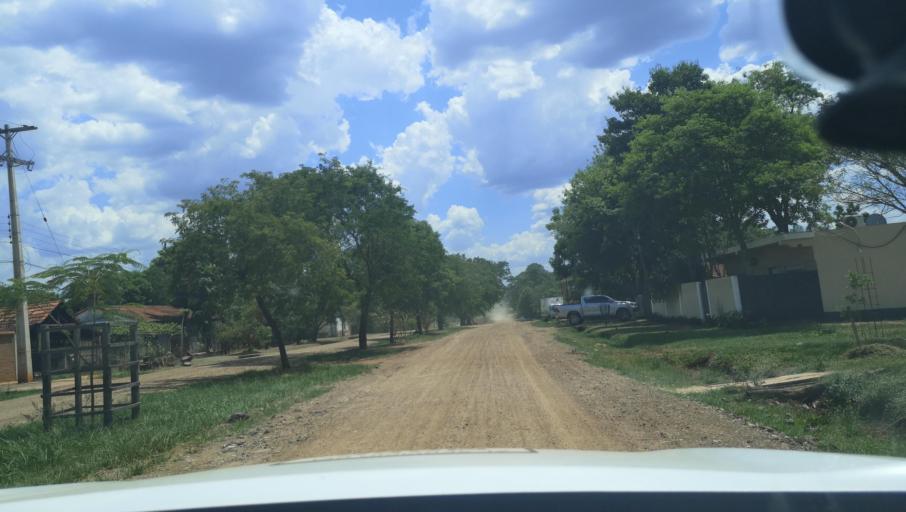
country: PY
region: Itapua
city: Carmen del Parana
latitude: -27.1538
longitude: -56.2413
